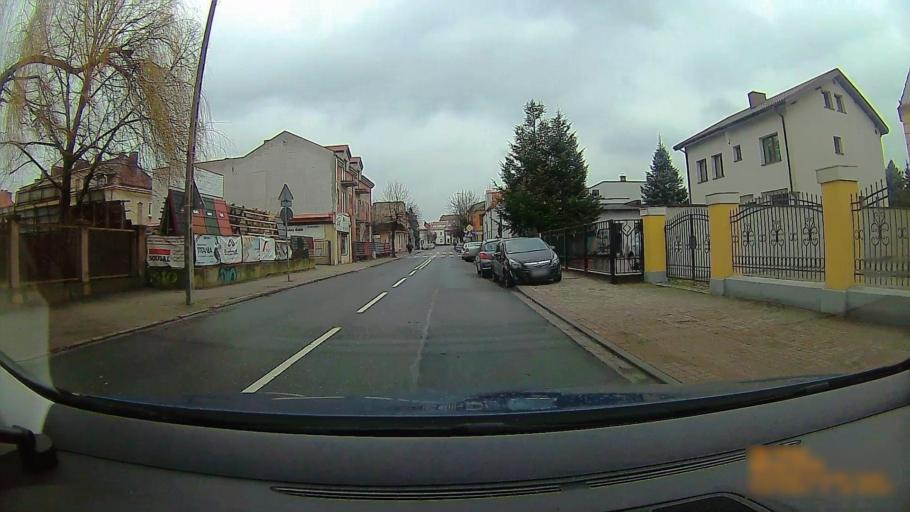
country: PL
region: Greater Poland Voivodeship
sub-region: Konin
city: Konin
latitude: 52.2106
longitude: 18.2502
